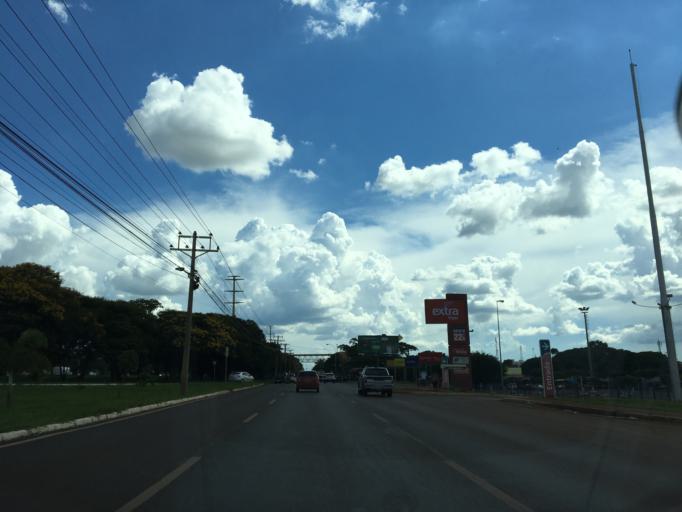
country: BR
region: Federal District
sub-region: Brasilia
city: Brasilia
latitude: -15.7935
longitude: -47.9447
